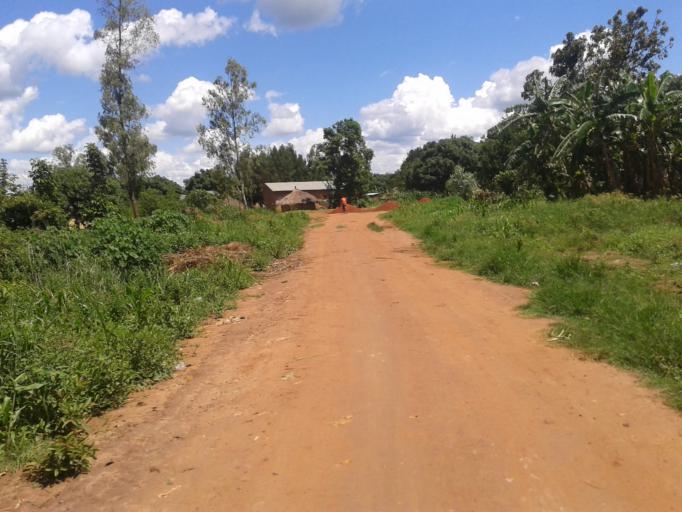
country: UG
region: Northern Region
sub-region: Gulu District
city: Gulu
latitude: 2.7656
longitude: 32.3195
